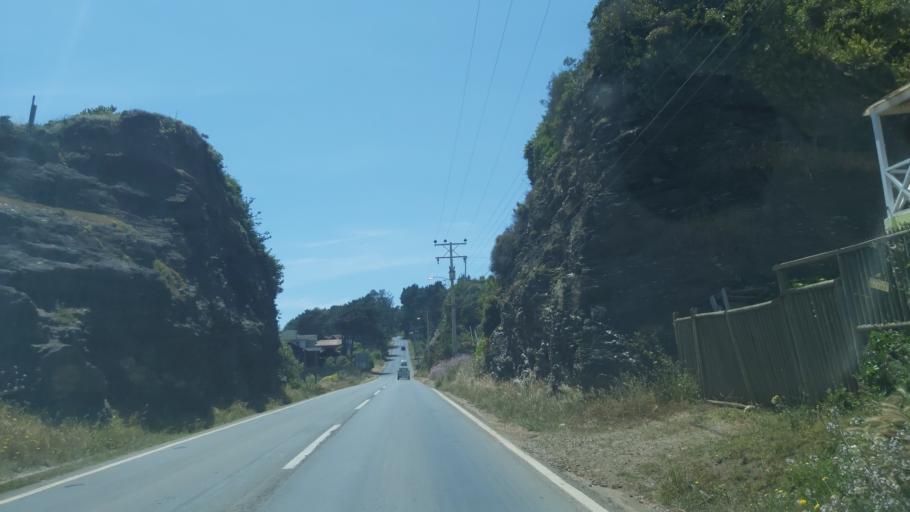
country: CL
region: Maule
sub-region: Provincia de Cauquenes
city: Cauquenes
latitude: -35.8365
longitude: -72.6241
